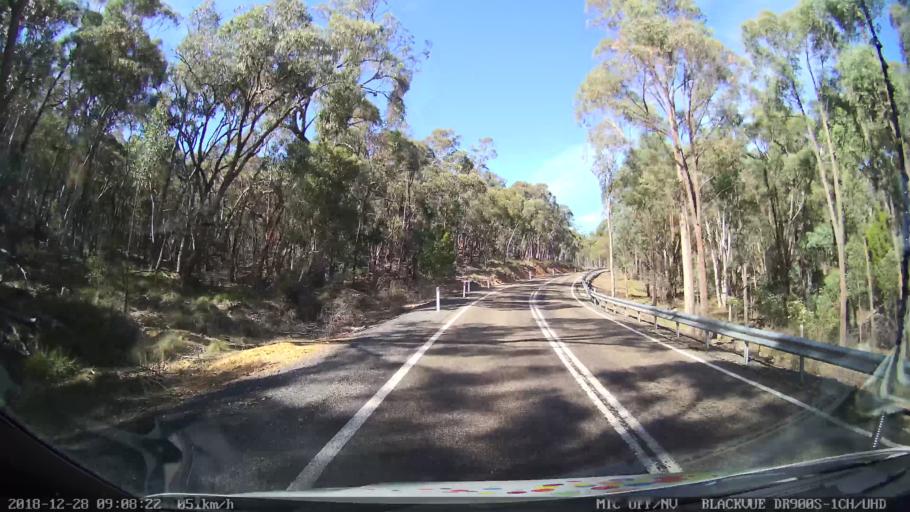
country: AU
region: New South Wales
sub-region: Upper Lachlan Shire
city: Crookwell
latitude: -34.2126
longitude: 149.3397
